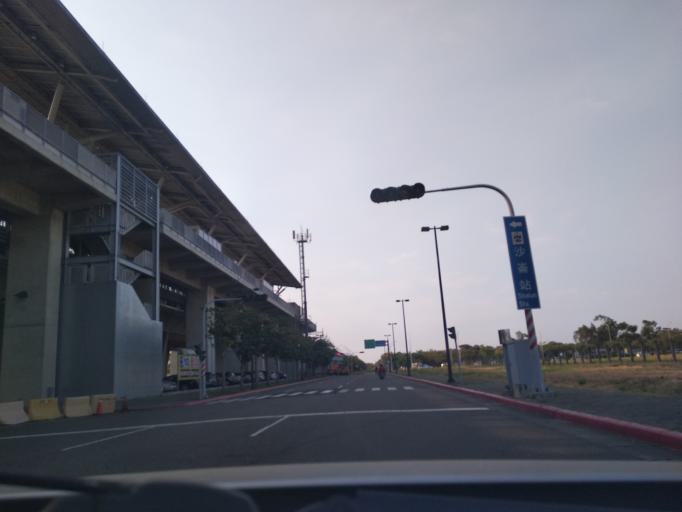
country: TW
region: Taiwan
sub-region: Tainan
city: Tainan
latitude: 22.9255
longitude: 120.2864
